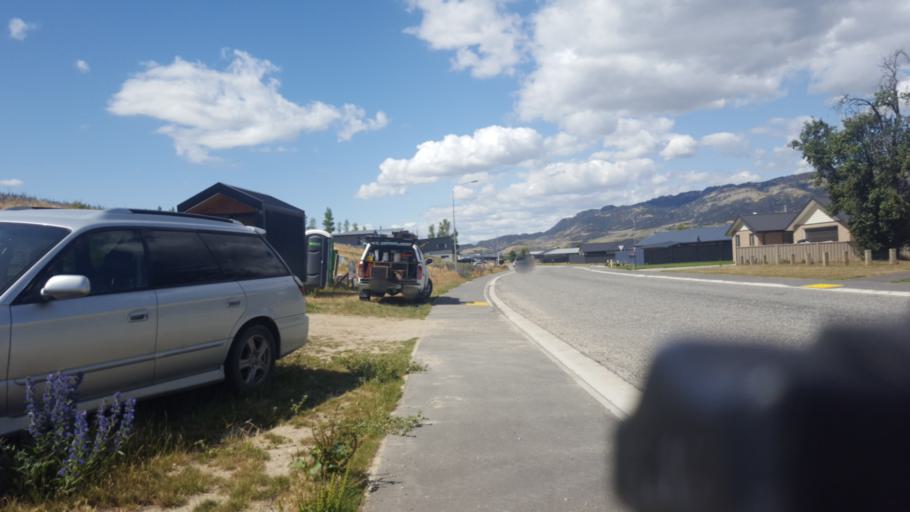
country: NZ
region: Otago
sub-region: Queenstown-Lakes District
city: Wanaka
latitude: -44.9748
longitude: 169.2403
